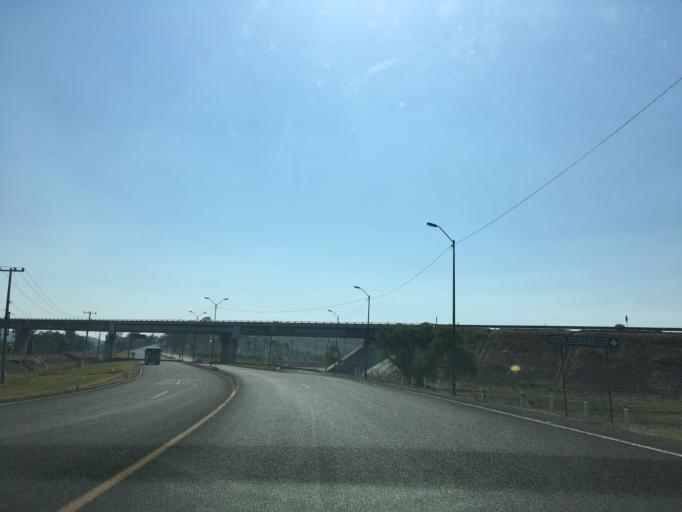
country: MX
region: Michoacan
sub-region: Morelia
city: La Aldea
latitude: 19.7361
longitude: -101.1049
